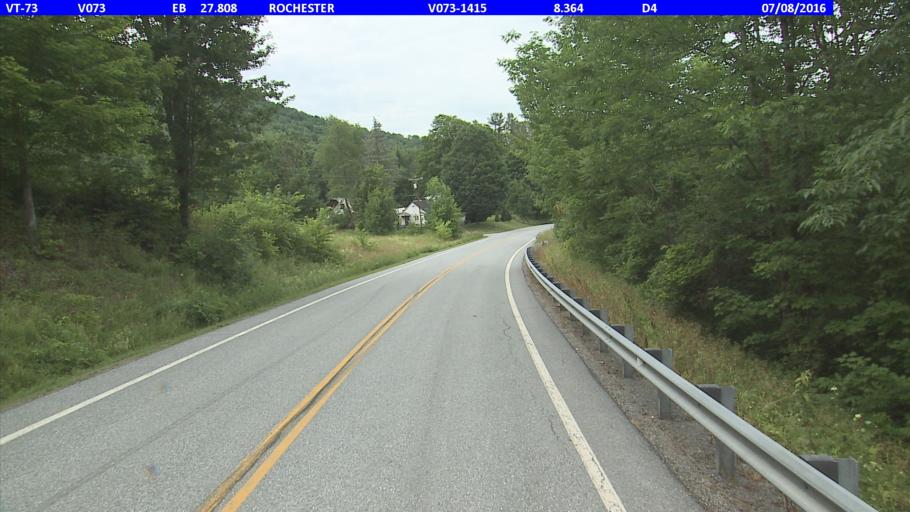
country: US
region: Vermont
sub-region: Orange County
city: Randolph
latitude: 43.8604
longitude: -72.8160
